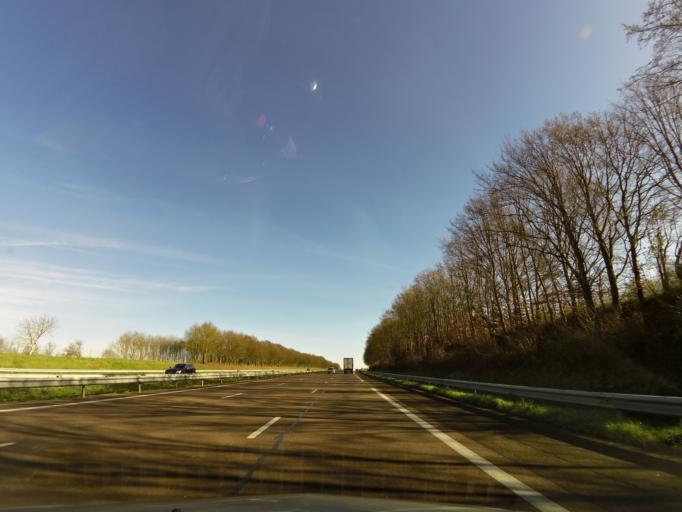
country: FR
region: Bourgogne
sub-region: Departement de l'Yonne
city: Fleury-la-Vallee
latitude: 47.8789
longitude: 3.4608
